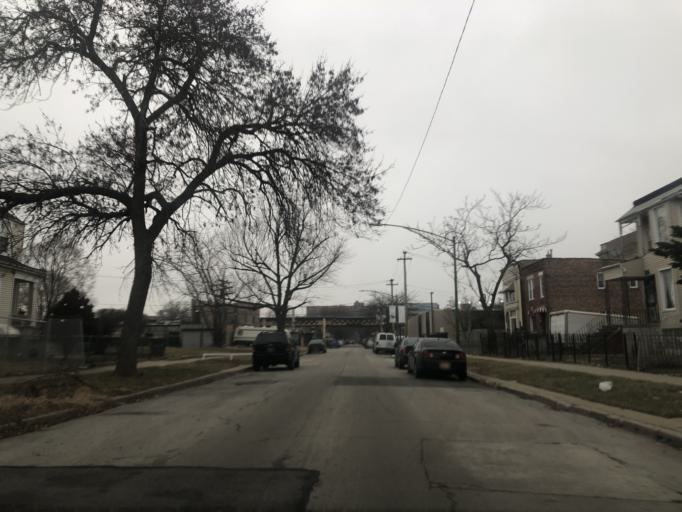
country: US
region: Illinois
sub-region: Cook County
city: Chicago
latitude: 41.7790
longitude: -87.6071
